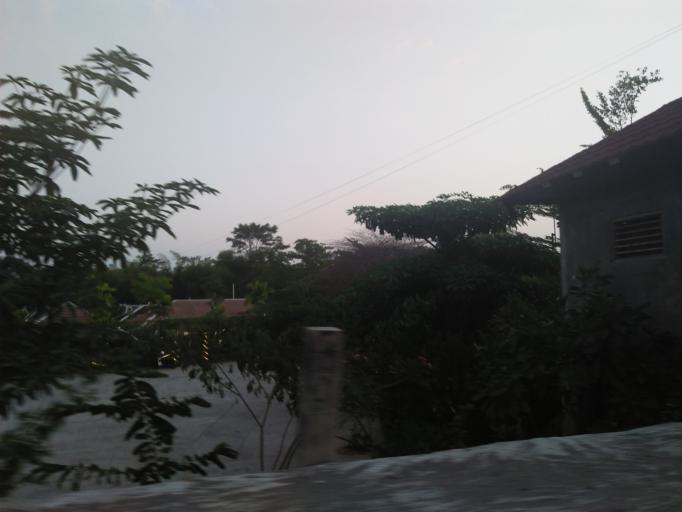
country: ID
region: Daerah Istimewa Yogyakarta
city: Sewon
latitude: -7.8437
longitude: 110.3959
